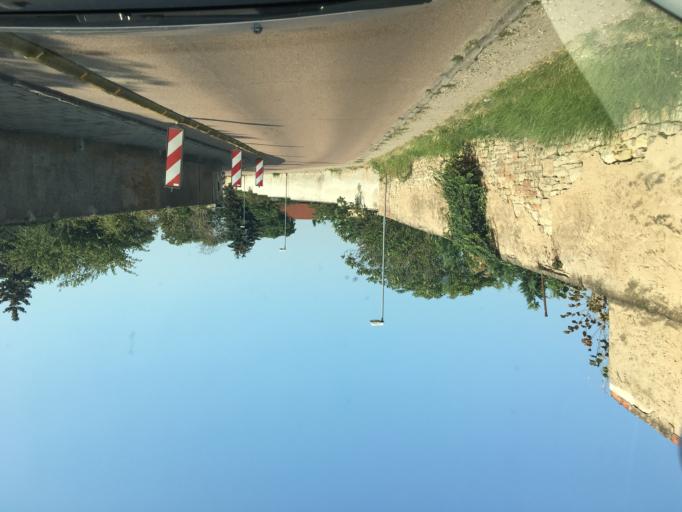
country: DE
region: Saxony-Anhalt
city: Nienburg/Saale
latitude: 51.8242
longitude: 11.7562
